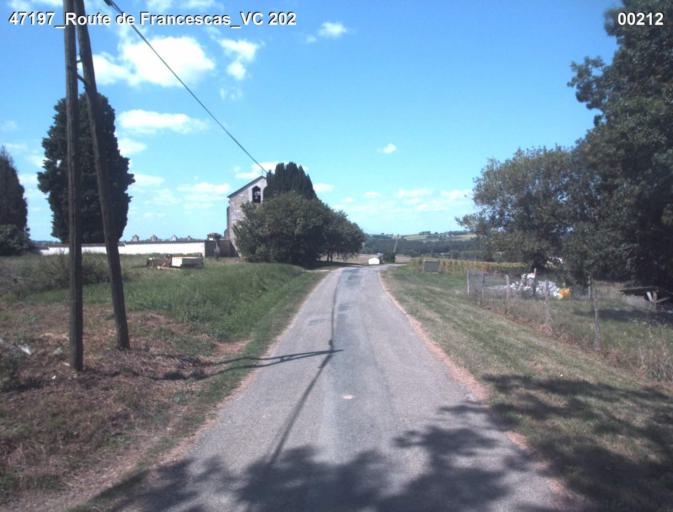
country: FR
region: Aquitaine
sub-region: Departement du Lot-et-Garonne
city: Laplume
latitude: 44.0658
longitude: 0.4721
